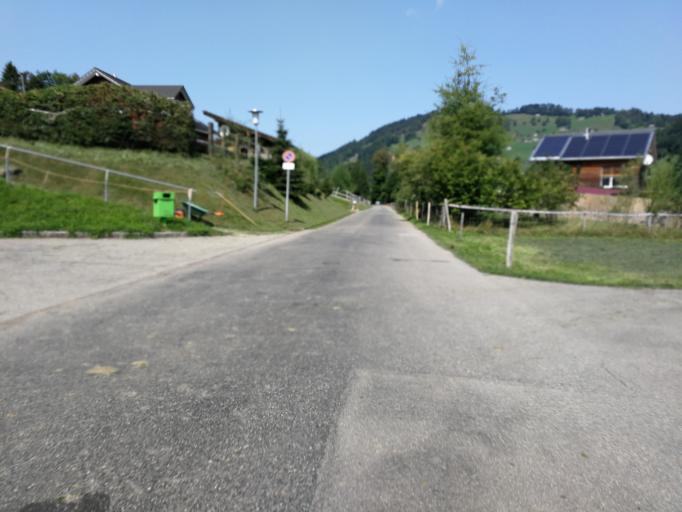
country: CH
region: Saint Gallen
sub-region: Wahlkreis Toggenburg
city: Krummenau
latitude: 47.2440
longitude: 9.1691
